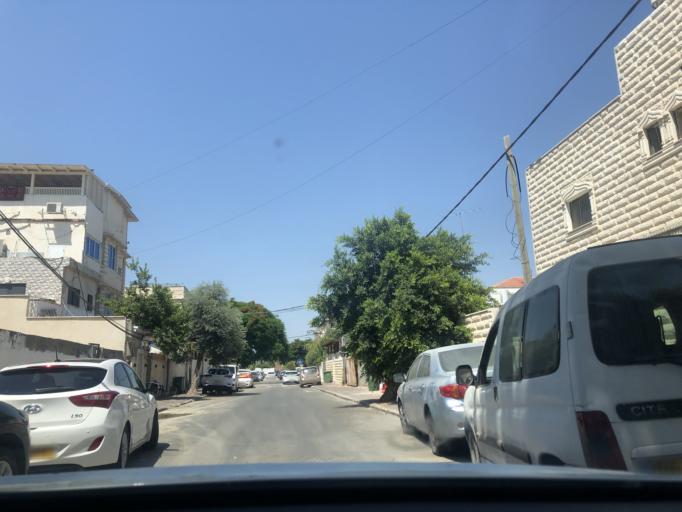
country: IL
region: Central District
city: Lod
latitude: 31.9584
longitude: 34.9025
